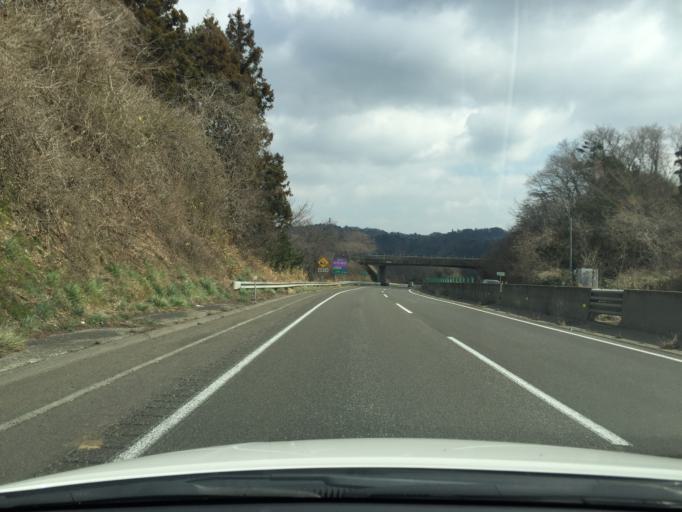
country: JP
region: Miyagi
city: Sendai
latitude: 38.2313
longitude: 140.8104
